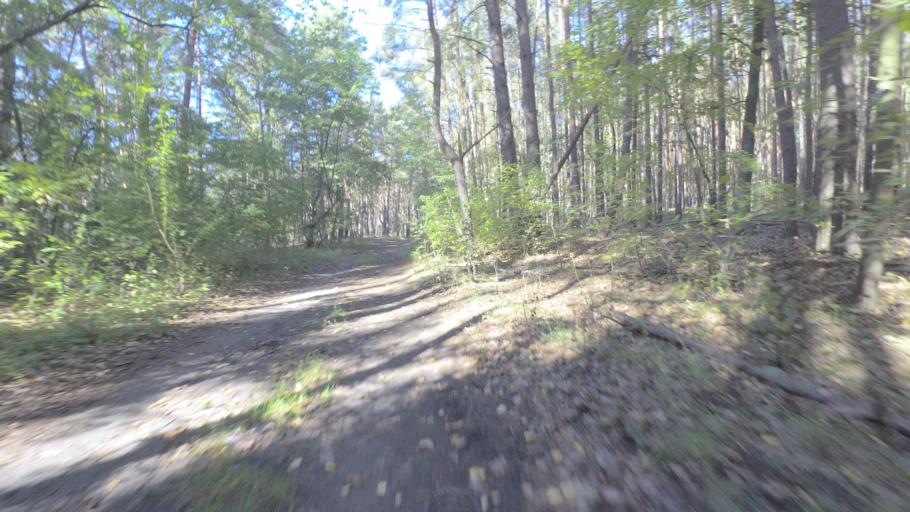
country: DE
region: Brandenburg
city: Sperenberg
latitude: 52.1517
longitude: 13.3427
